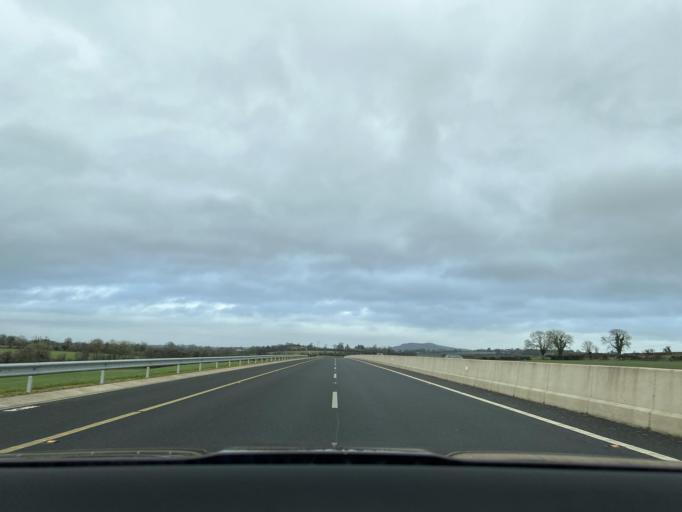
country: IE
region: Leinster
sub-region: Loch Garman
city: Ferns
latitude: 52.5592
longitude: -6.4700
